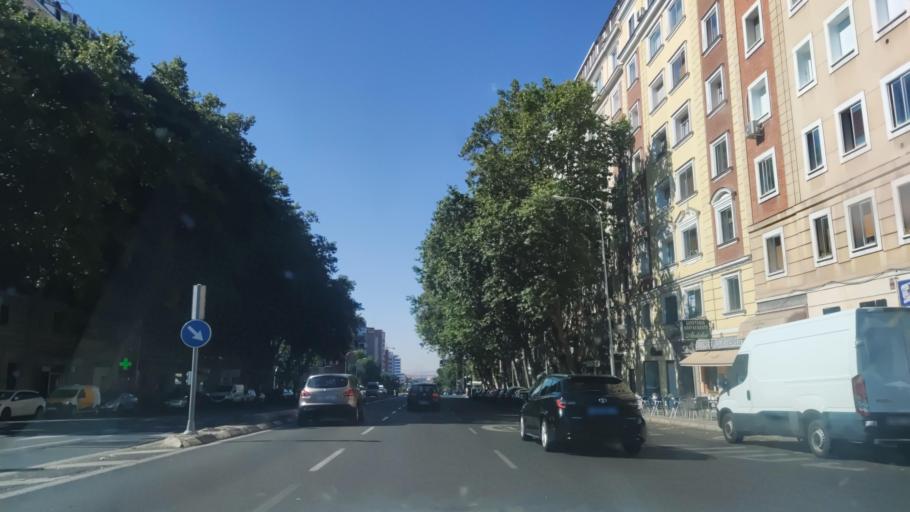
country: ES
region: Madrid
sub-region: Provincia de Madrid
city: Retiro
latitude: 40.4179
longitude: -3.6693
